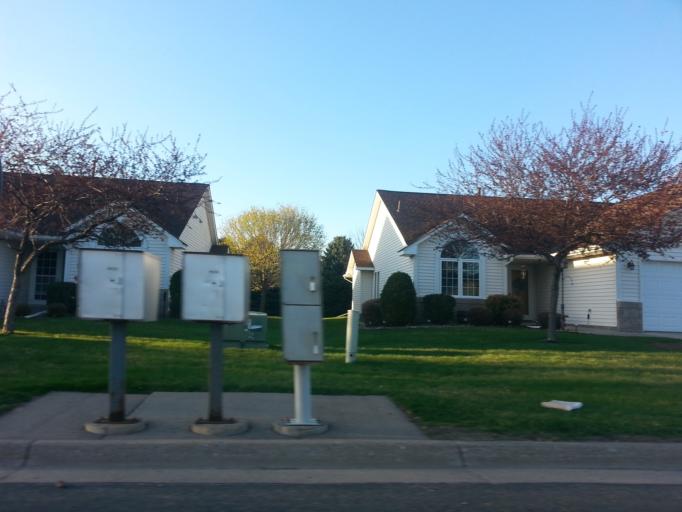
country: US
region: Minnesota
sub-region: Dakota County
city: Hastings
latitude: 44.7089
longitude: -92.8345
